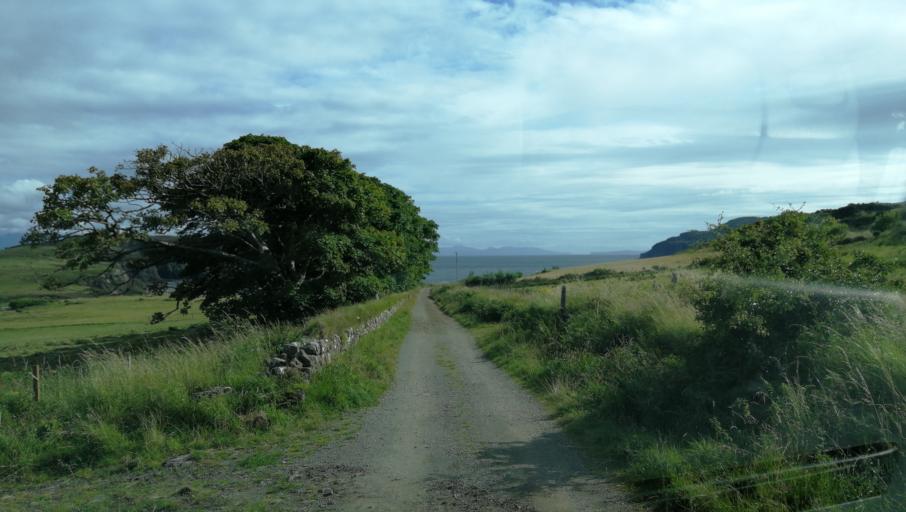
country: GB
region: Scotland
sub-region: Highland
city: Isle of Skye
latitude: 57.3944
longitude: -6.5661
